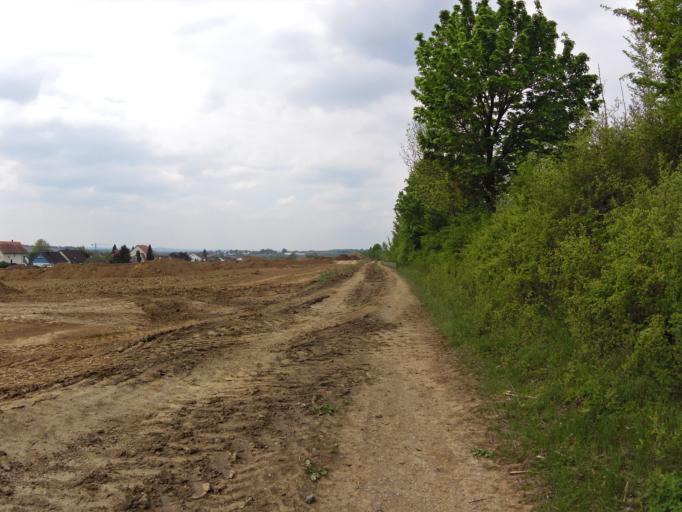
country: DE
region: Bavaria
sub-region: Regierungsbezirk Unterfranken
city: Kurnach
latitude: 49.8524
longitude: 10.0479
